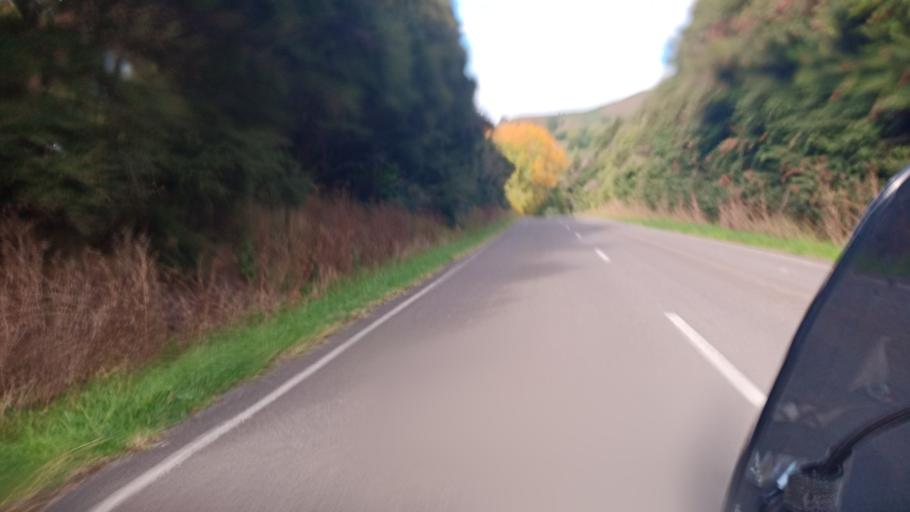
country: NZ
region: Gisborne
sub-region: Gisborne District
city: Gisborne
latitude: -38.5915
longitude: 177.7785
